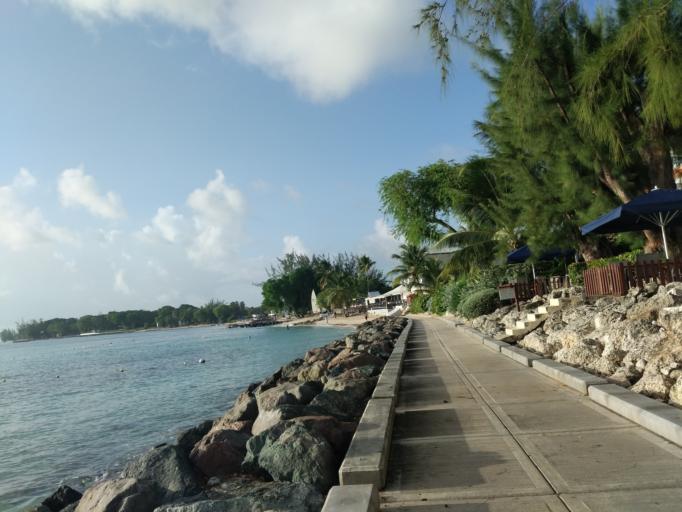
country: BB
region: Saint James
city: Holetown
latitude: 13.1839
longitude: -59.6389
